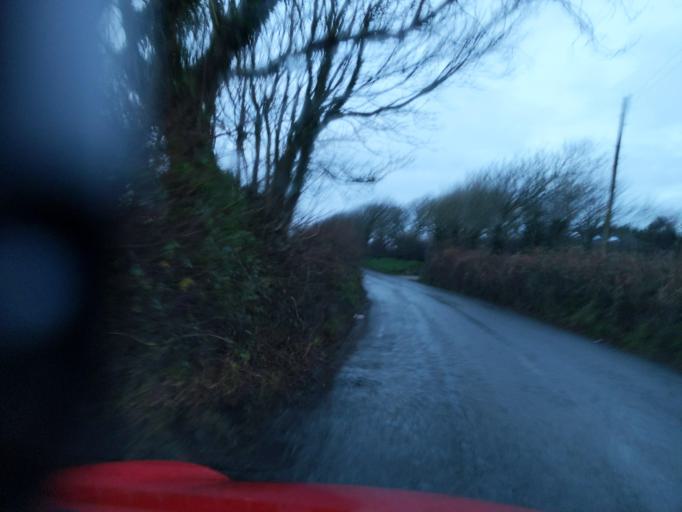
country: GB
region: England
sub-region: Devon
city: Wembury
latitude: 50.3322
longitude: -4.0648
